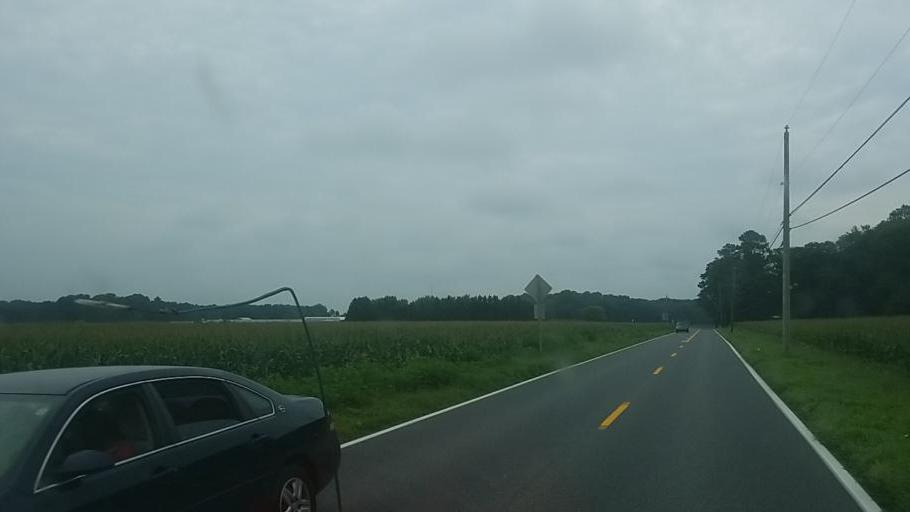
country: US
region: Delaware
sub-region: Sussex County
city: Selbyville
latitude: 38.4496
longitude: -75.1878
